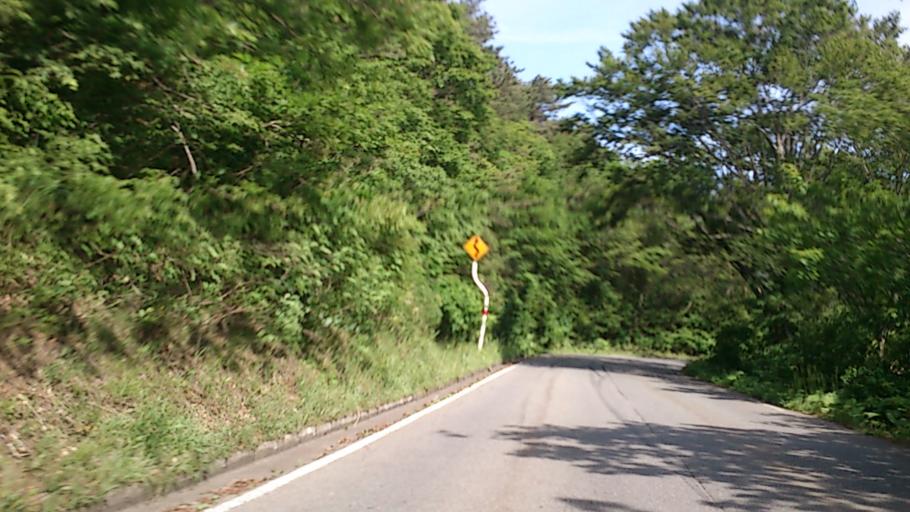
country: JP
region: Aomori
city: Aomori Shi
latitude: 40.7146
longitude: 140.8209
